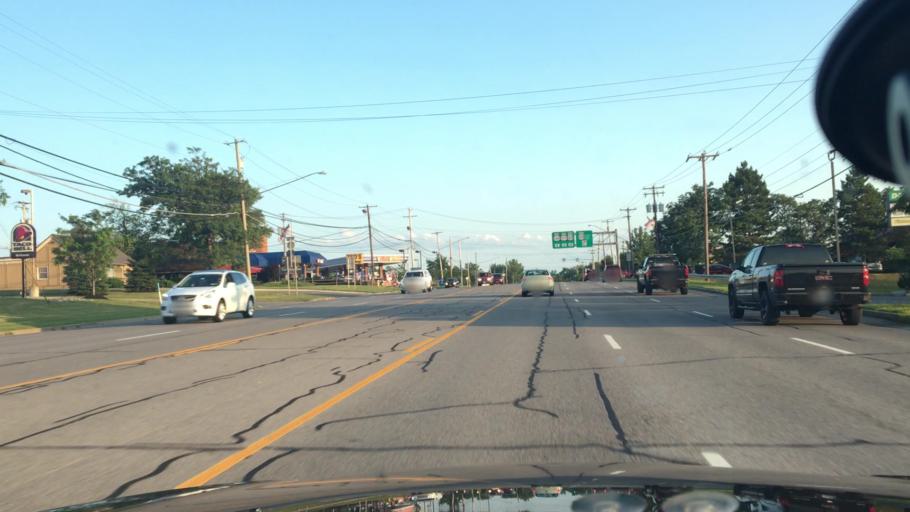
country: US
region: New York
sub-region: Erie County
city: Orchard Park
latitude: 42.7990
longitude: -78.7517
